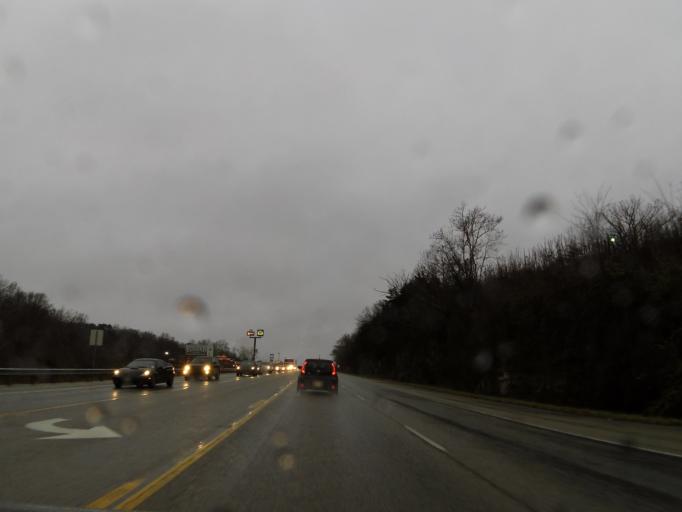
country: US
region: Kentucky
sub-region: Rockcastle County
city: Mount Vernon
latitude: 37.3731
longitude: -84.3337
